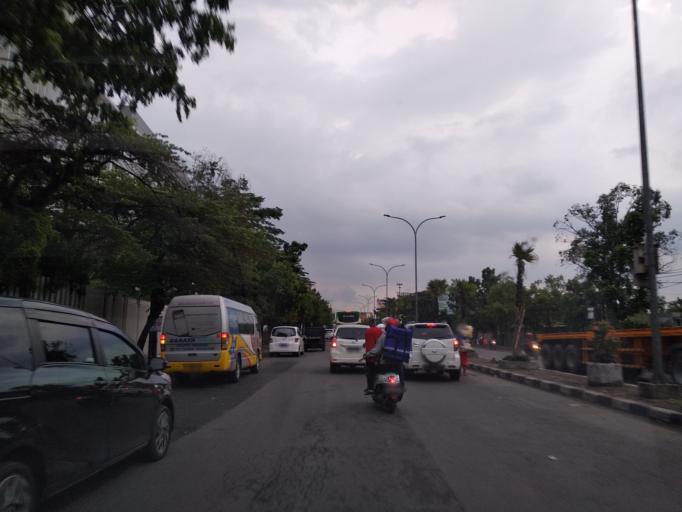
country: ID
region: West Java
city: Bandung
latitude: -6.9497
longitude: 107.6350
